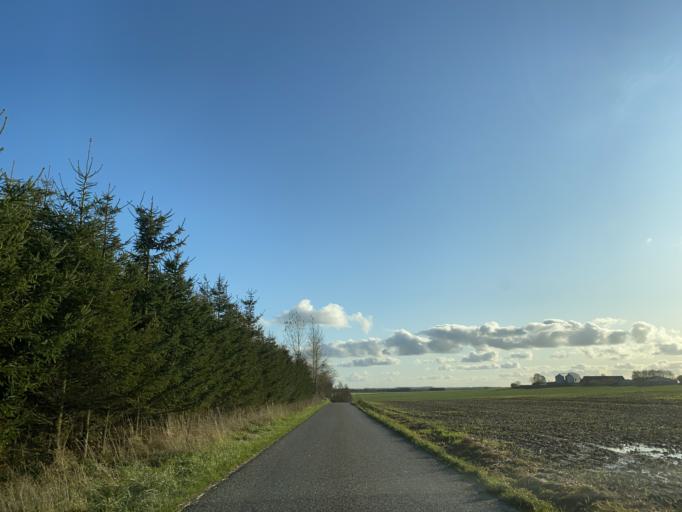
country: DK
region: Central Jutland
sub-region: Viborg Kommune
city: Bjerringbro
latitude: 56.3391
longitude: 9.7148
